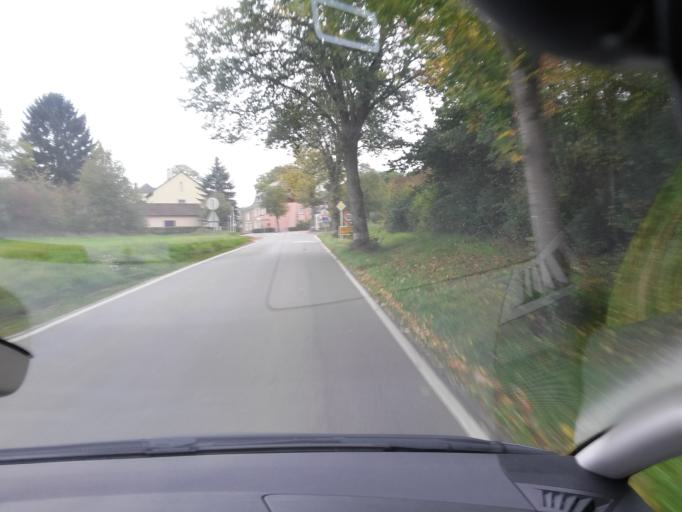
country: LU
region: Diekirch
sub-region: Canton de Redange
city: Beckerich
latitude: 49.7255
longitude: 5.8992
